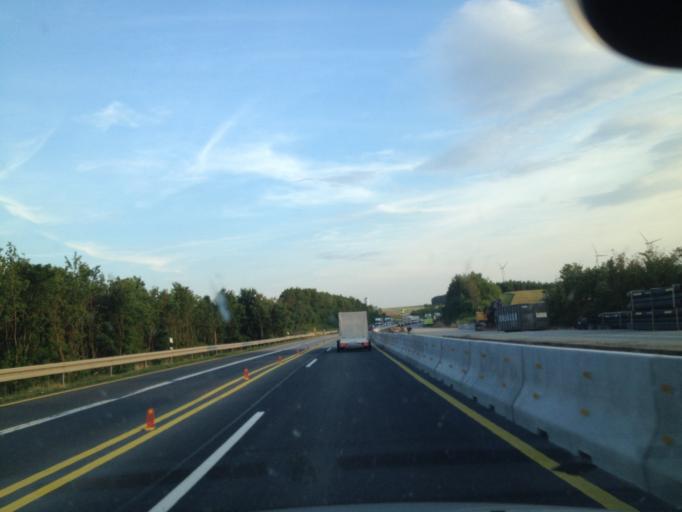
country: DE
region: Bavaria
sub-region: Regierungsbezirk Mittelfranken
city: Gollhofen
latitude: 49.5712
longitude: 10.1726
